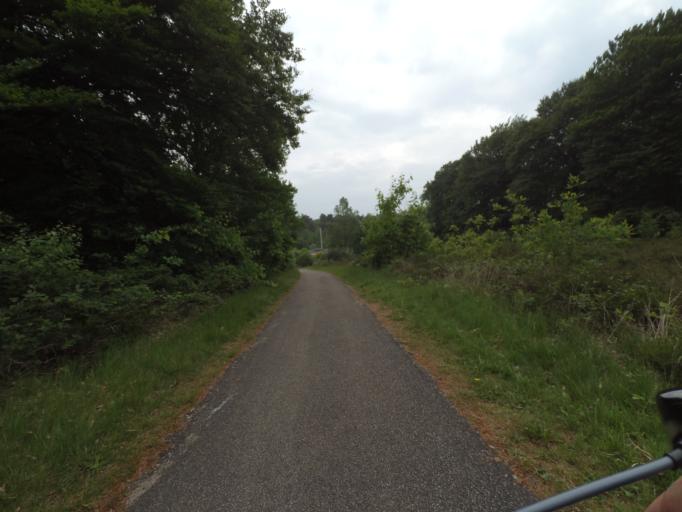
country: NL
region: Gelderland
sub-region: Gemeente Renkum
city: Wolfheze
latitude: 52.0013
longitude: 5.8004
